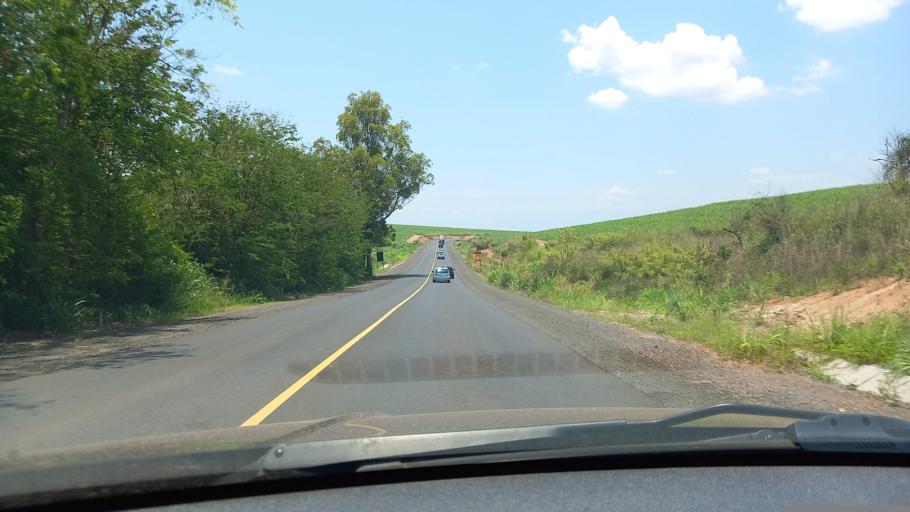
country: BR
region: Sao Paulo
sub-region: Moji-Guacu
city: Mogi-Gaucu
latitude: -22.3547
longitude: -46.8707
